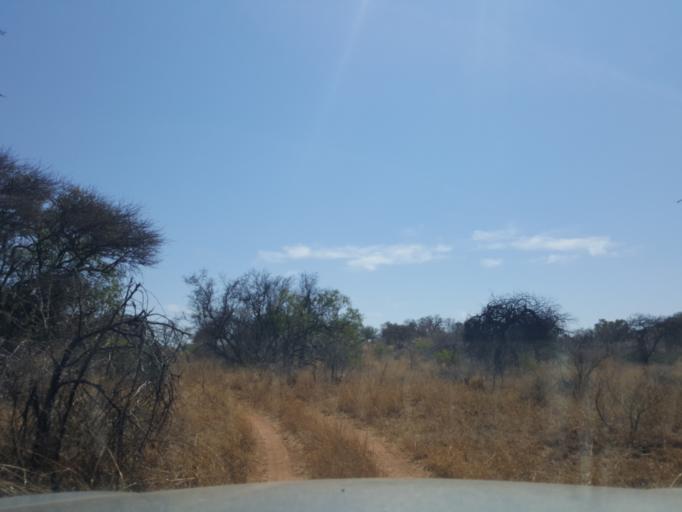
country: BW
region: South East
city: Lobatse
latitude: -25.1354
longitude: 25.6727
